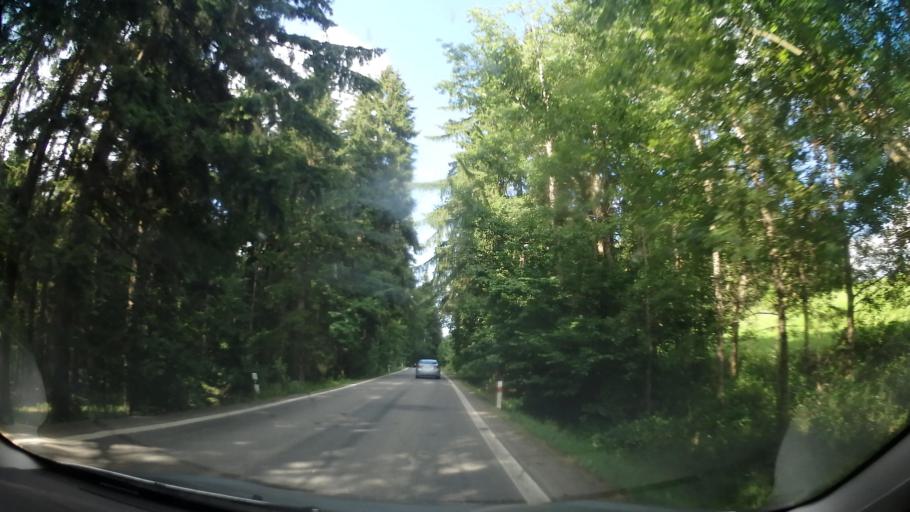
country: CZ
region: Vysocina
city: Zd'ar nad Sazavou Druhy
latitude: 49.6149
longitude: 15.9354
